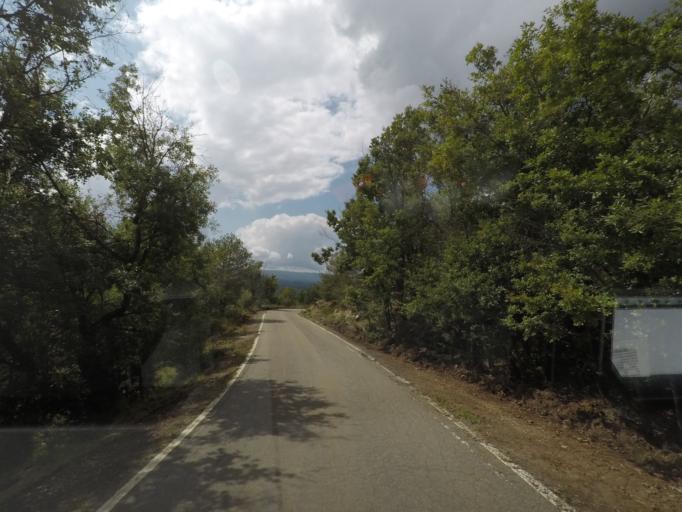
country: ES
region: Aragon
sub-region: Provincia de Huesca
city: Fiscal
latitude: 42.4126
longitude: -0.1234
